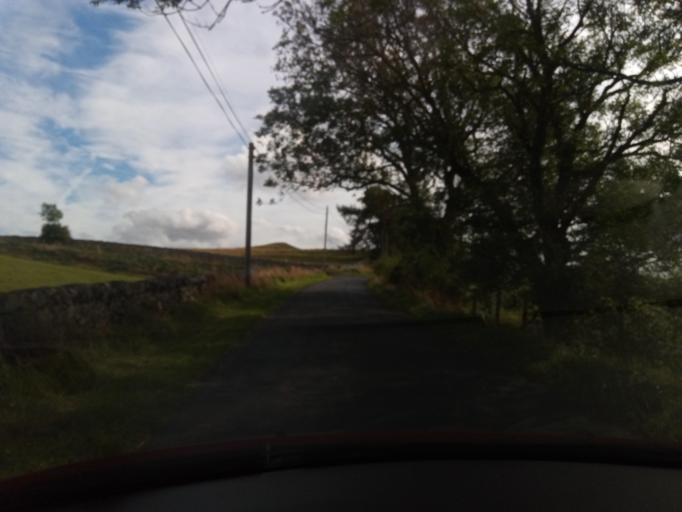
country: GB
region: Scotland
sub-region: The Scottish Borders
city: Kelso
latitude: 55.4777
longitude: -2.3535
